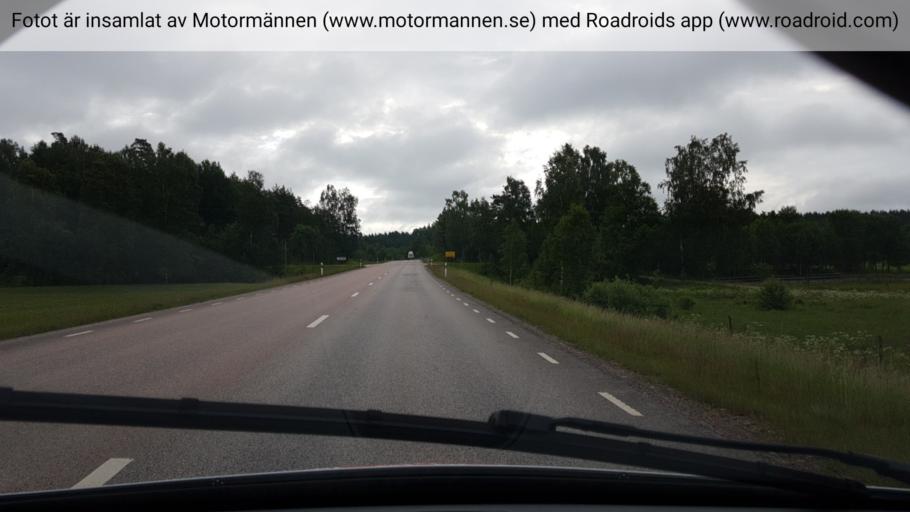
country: SE
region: Vaestra Goetaland
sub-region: Tibro Kommun
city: Tibro
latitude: 58.4547
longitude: 14.2493
